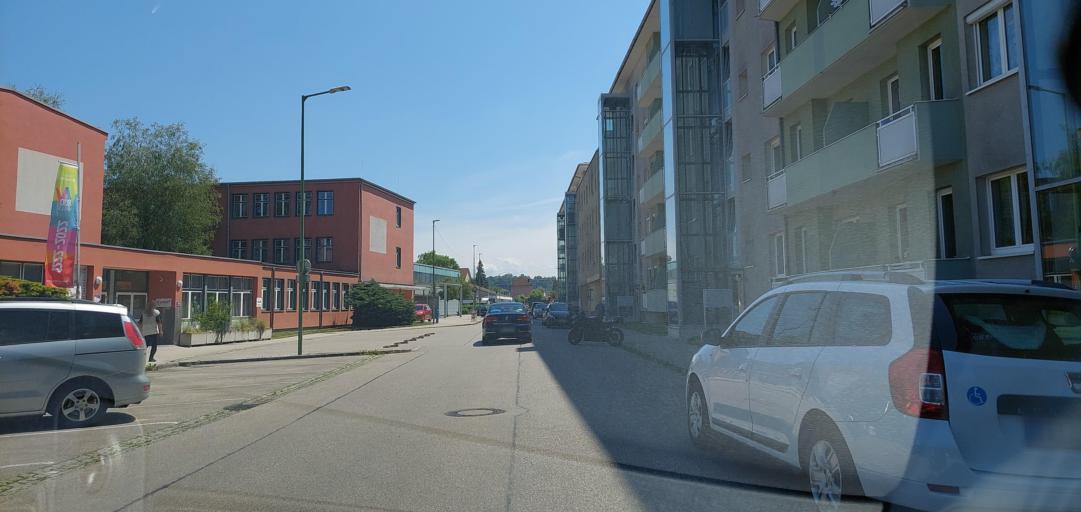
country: AT
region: Upper Austria
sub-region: Wels Stadt
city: Wels
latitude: 48.1620
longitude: 14.0061
